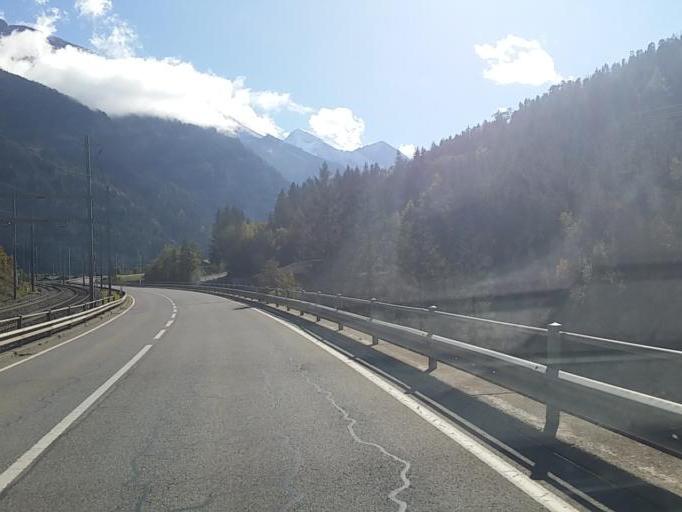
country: CH
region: Bern
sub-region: Frutigen-Niedersimmental District
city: Kandersteg
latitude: 46.5080
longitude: 7.6747
